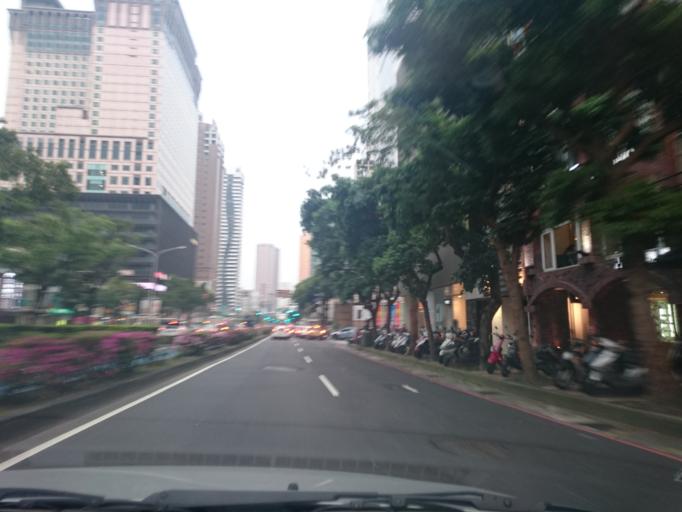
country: TW
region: Taiwan
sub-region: Taichung City
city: Taichung
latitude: 24.1559
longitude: 120.6615
